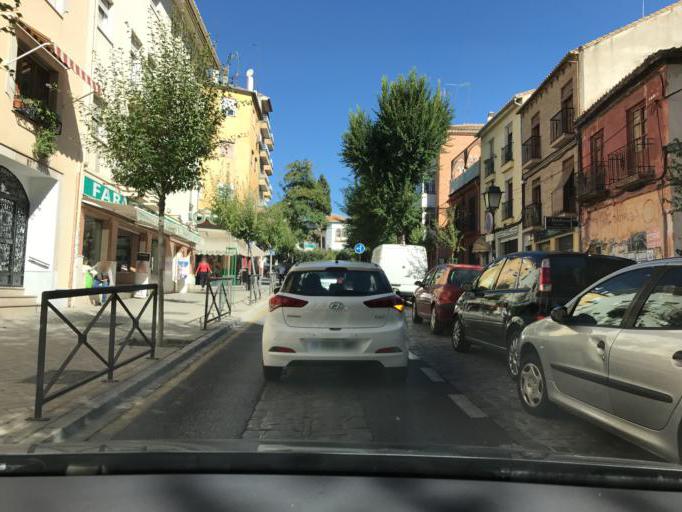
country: ES
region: Andalusia
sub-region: Provincia de Granada
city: Granada
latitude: 37.1869
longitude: -3.6000
